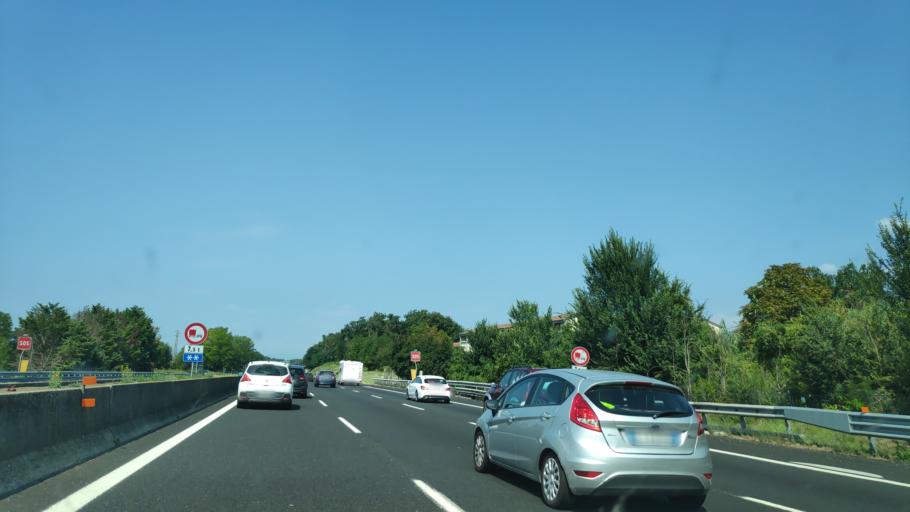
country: IT
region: Latium
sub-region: Provincia di Frosinone
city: Pignataro Interamna
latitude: 41.4601
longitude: 13.7906
